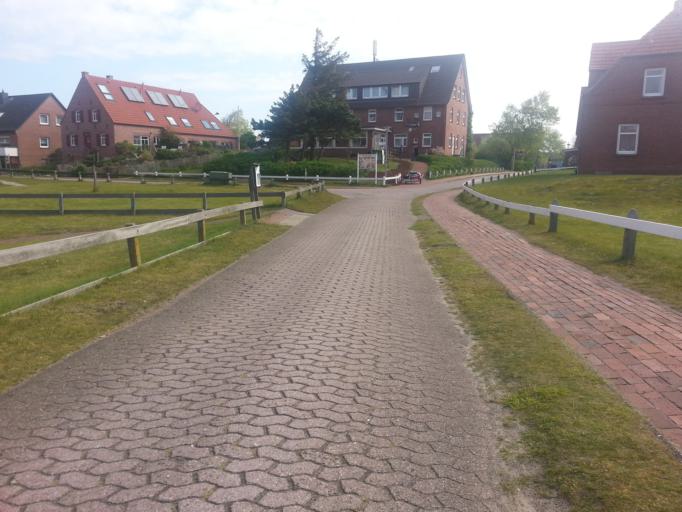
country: DE
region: Lower Saxony
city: Baltrum
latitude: 53.7276
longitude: 7.3715
